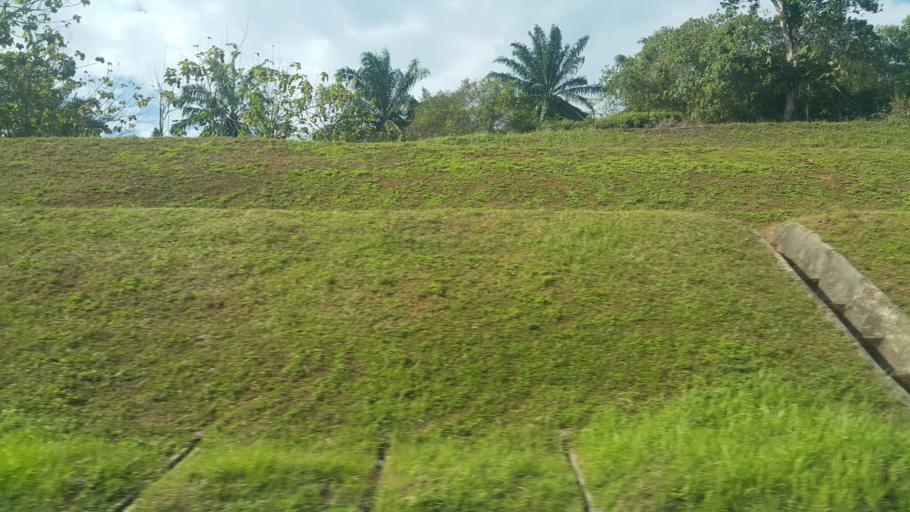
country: MY
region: Johor
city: Kulai
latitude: 1.6244
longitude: 103.5797
